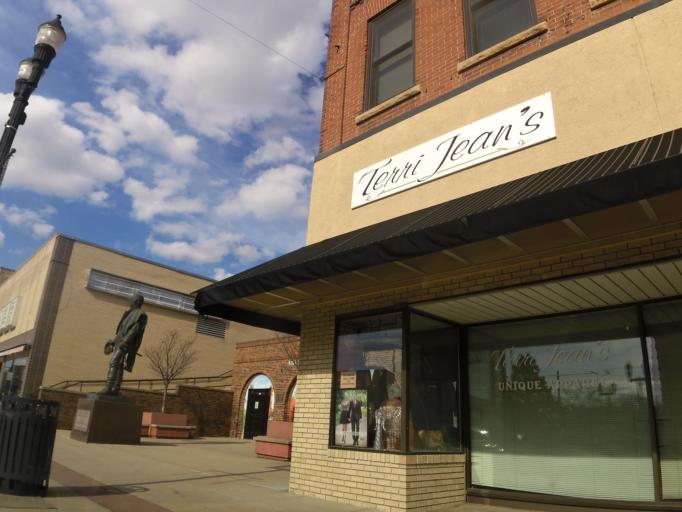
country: US
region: Minnesota
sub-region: Chippewa County
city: Montevideo
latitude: 44.9454
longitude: -95.7243
